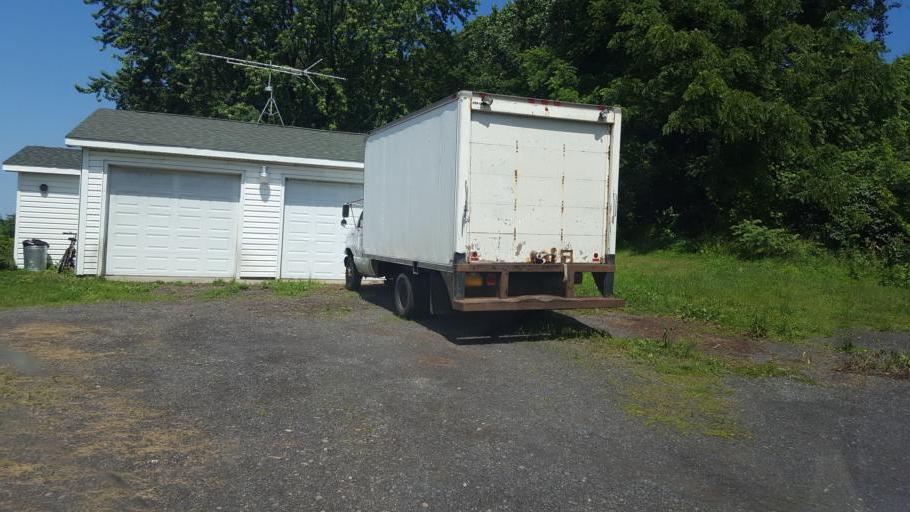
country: US
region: New York
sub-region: Wayne County
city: Wolcott
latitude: 43.2547
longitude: -76.9273
